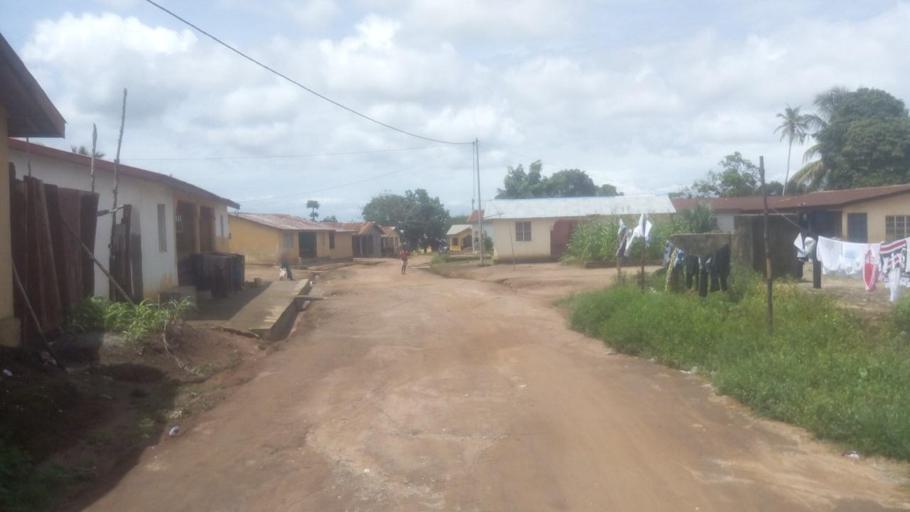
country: SL
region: Northern Province
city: Masoyila
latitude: 8.6022
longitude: -13.1820
